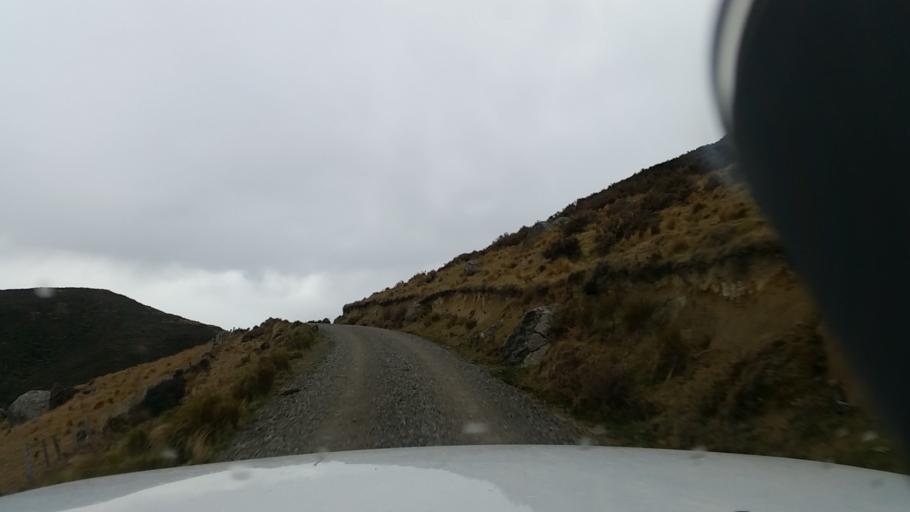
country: NZ
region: Canterbury
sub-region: Christchurch City
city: Christchurch
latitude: -43.8546
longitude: 172.8812
